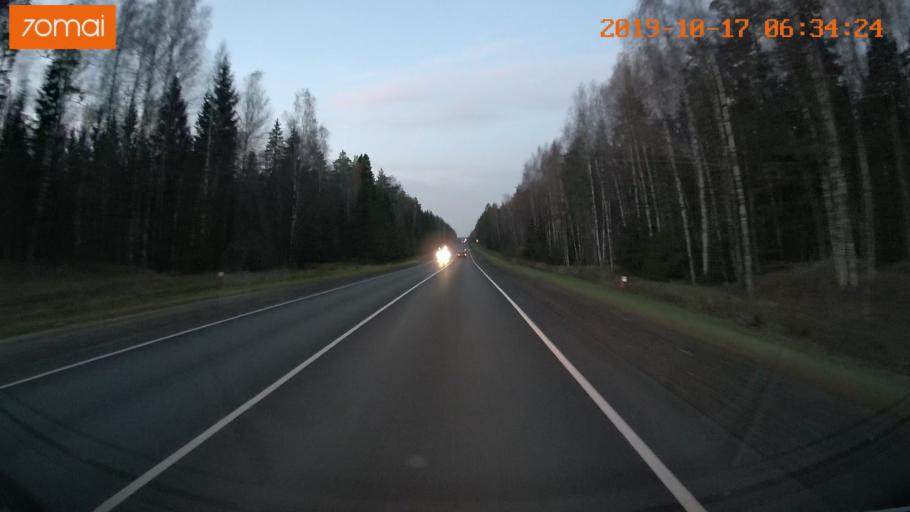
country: RU
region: Ivanovo
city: Novoye Leushino
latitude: 56.7037
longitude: 40.6393
